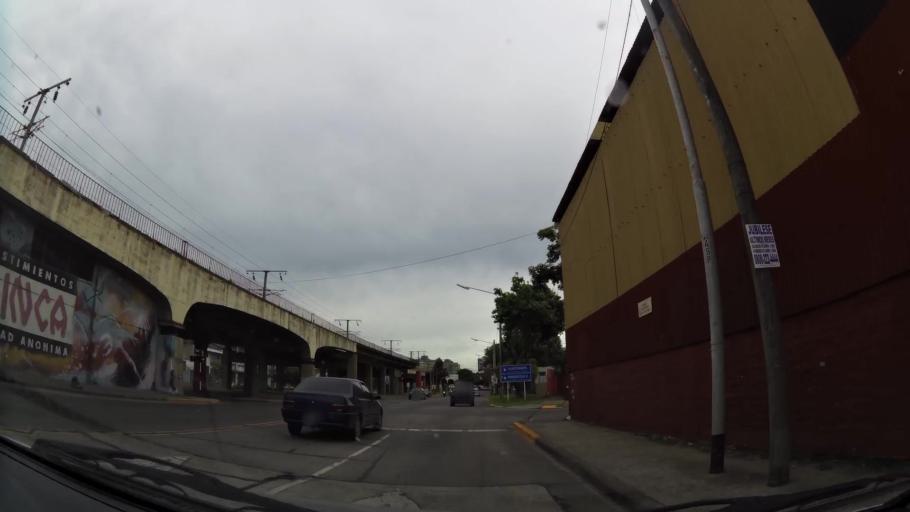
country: AR
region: Buenos Aires
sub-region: Partido de Avellaneda
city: Avellaneda
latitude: -34.6745
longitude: -58.3577
